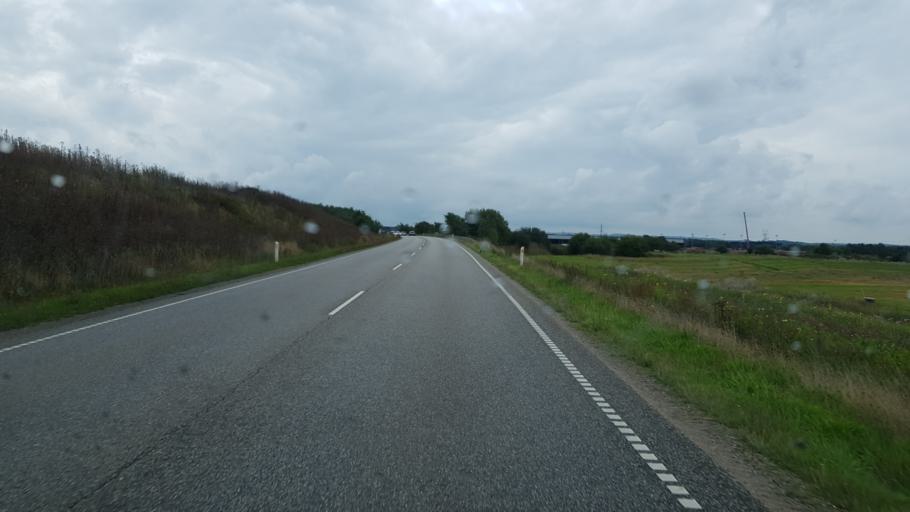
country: DK
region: Central Jutland
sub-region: Horsens Kommune
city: Horsens
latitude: 55.8926
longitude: 9.7604
